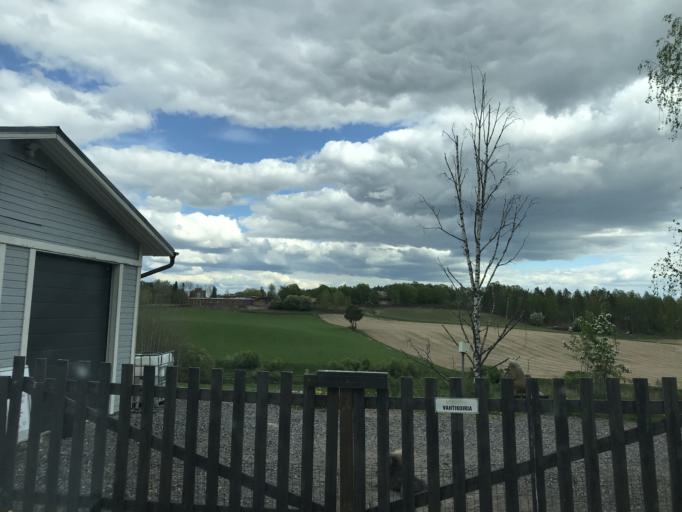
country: FI
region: Uusimaa
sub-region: Helsinki
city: Nurmijaervi
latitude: 60.4268
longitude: 24.7131
